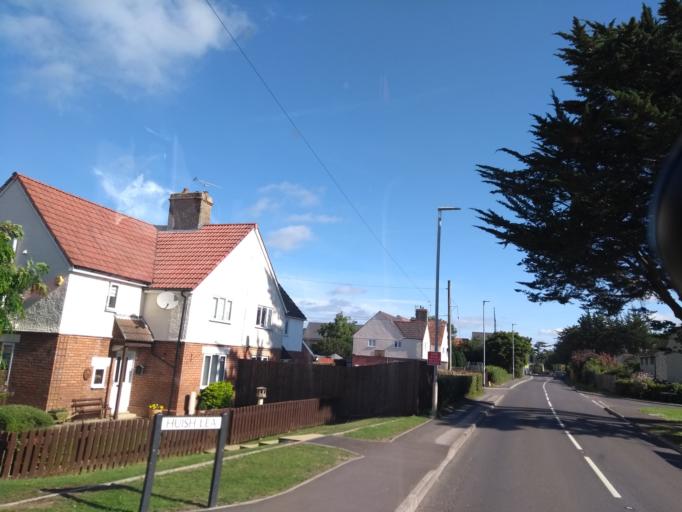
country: GB
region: England
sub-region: Somerset
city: Langport
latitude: 51.0417
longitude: -2.8193
